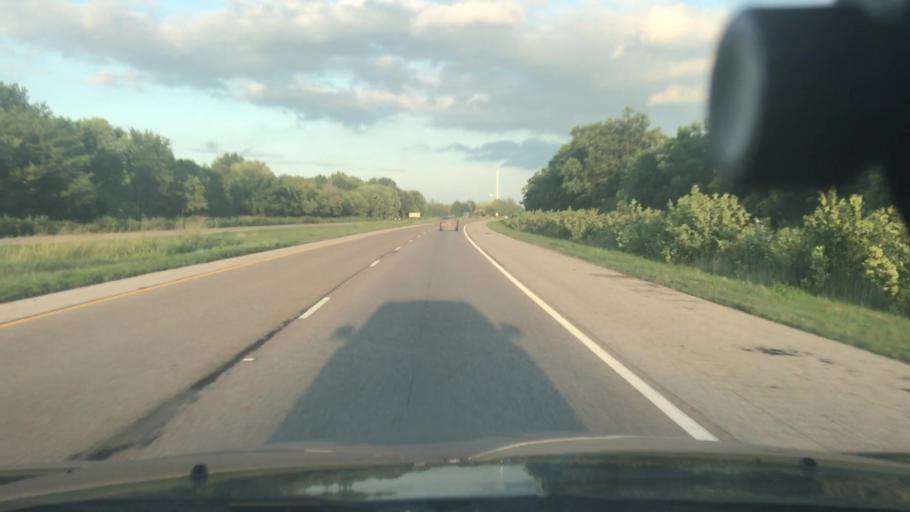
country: US
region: Illinois
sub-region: Clinton County
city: Albers
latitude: 38.5082
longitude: -89.6310
